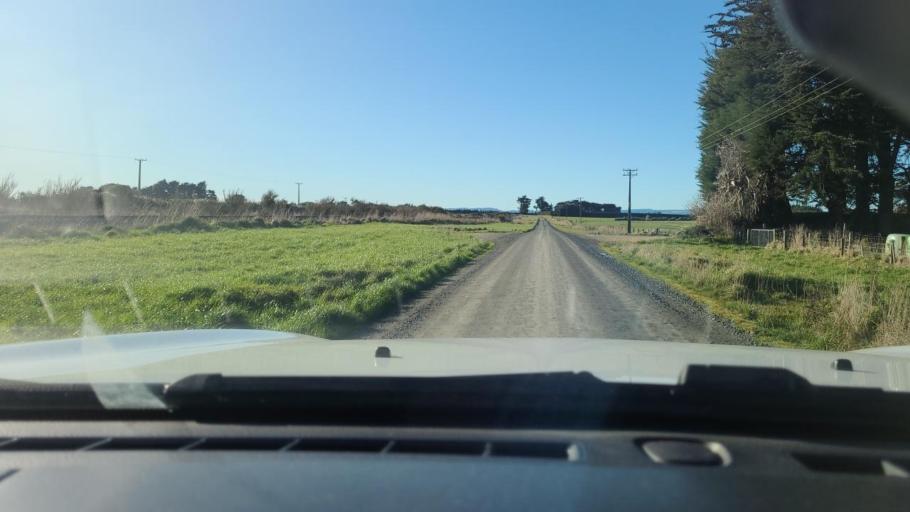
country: NZ
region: Southland
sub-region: Invercargill City
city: Invercargill
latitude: -46.3413
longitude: 168.6553
